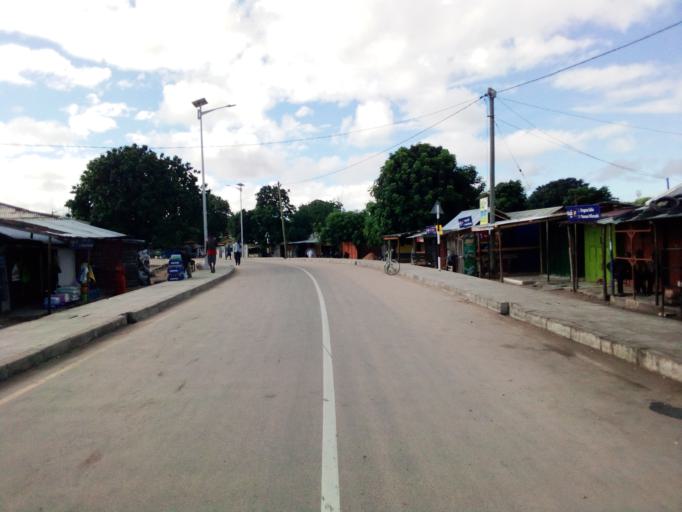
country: TZ
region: Dodoma
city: Dodoma
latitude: -6.1804
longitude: 35.7398
